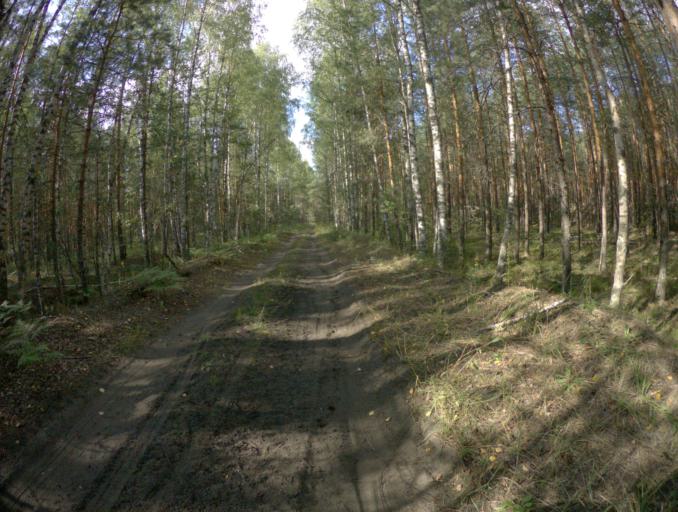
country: RU
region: Vladimir
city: Sobinka
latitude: 55.9502
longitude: 40.0590
